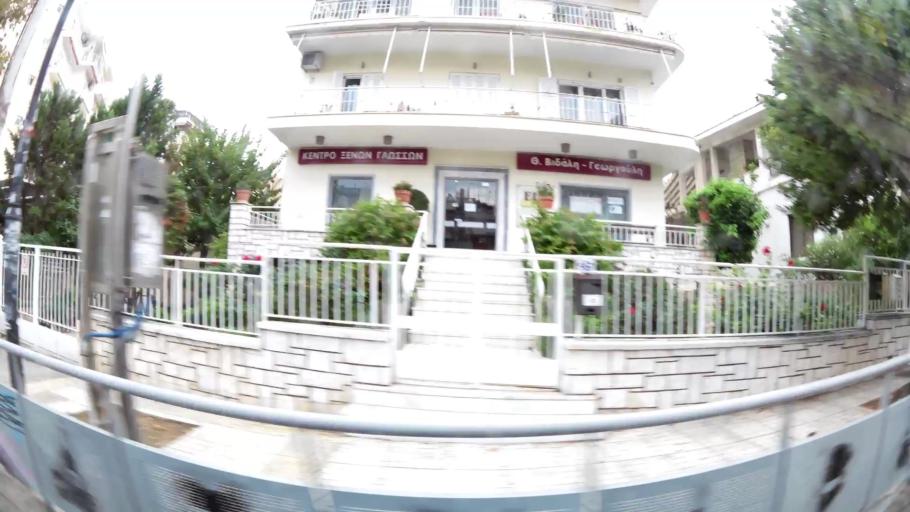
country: GR
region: Attica
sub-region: Nomarchia Athinas
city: Palaio Faliro
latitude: 37.9246
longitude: 23.7014
